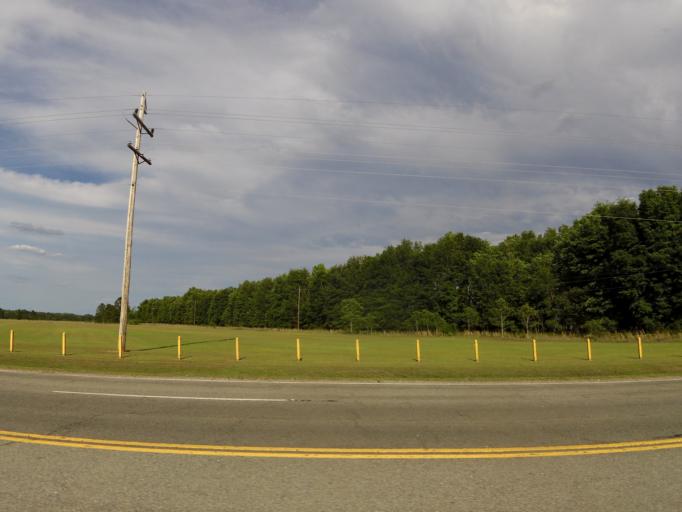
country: US
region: South Carolina
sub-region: Hampton County
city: Estill
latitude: 32.7888
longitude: -81.2405
